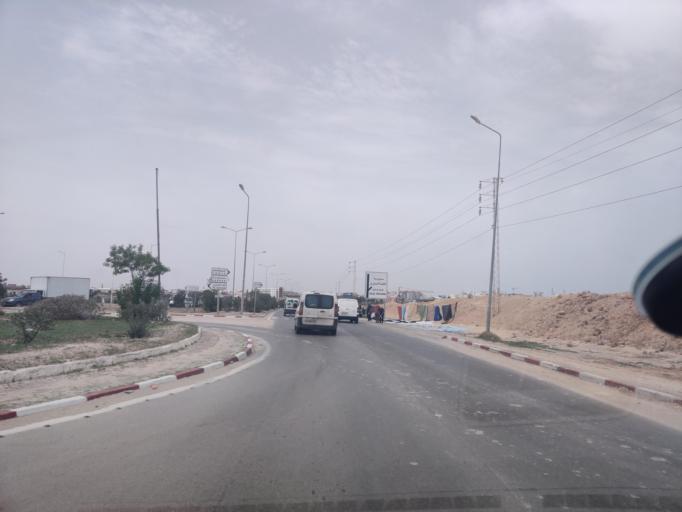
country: TN
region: Susah
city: Hammam Sousse
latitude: 35.8210
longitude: 10.5951
